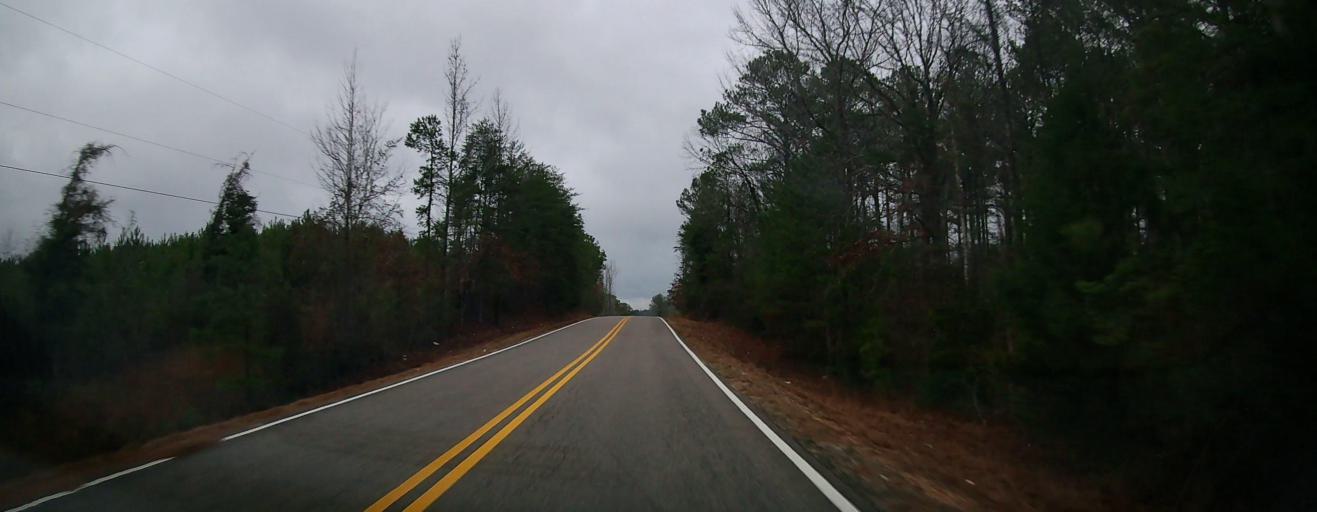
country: US
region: Alabama
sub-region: Bibb County
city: Centreville
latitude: 33.0166
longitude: -87.1462
